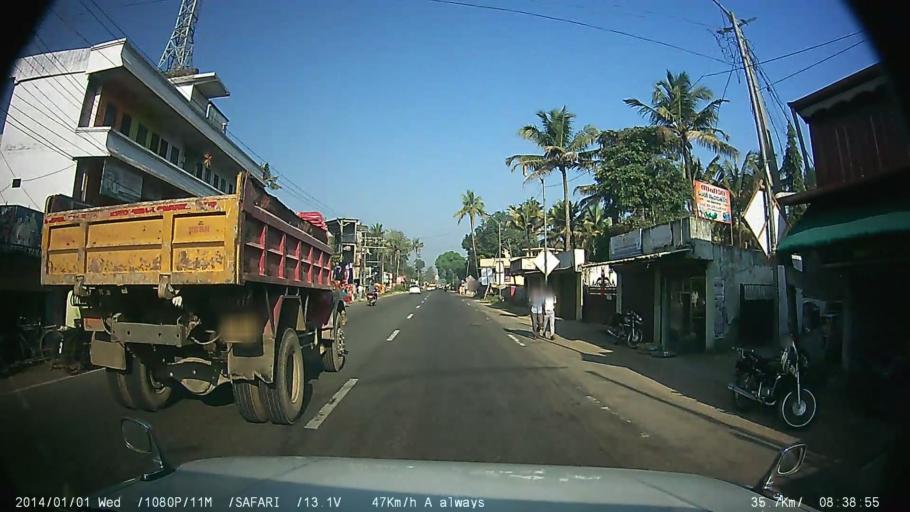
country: IN
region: Kerala
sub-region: Ernakulam
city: Perumpavur
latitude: 10.1528
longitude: 76.4503
